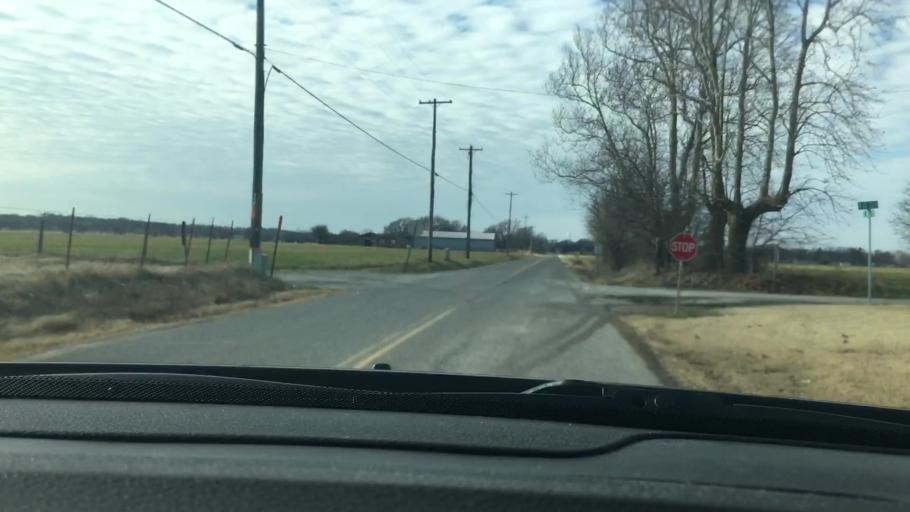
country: US
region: Oklahoma
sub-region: Garvin County
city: Pauls Valley
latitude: 34.7388
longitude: -97.1950
